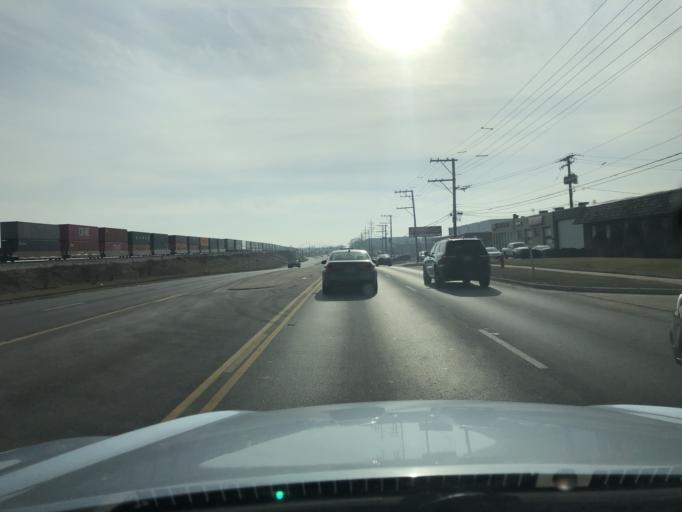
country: US
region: Illinois
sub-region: DuPage County
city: Bensenville
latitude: 41.9655
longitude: -87.9397
